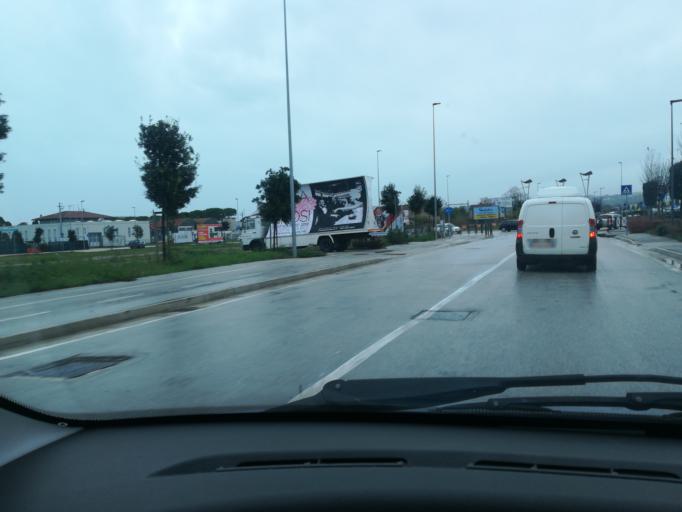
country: IT
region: The Marches
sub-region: Provincia di Macerata
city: Santa Maria Apparente
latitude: 43.2949
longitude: 13.7023
